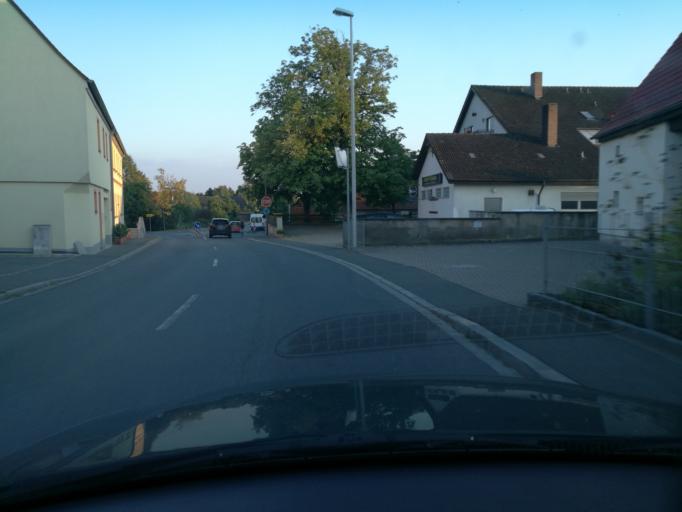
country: DE
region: Bavaria
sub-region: Regierungsbezirk Mittelfranken
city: Herzogenaurach
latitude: 49.5927
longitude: 10.8949
